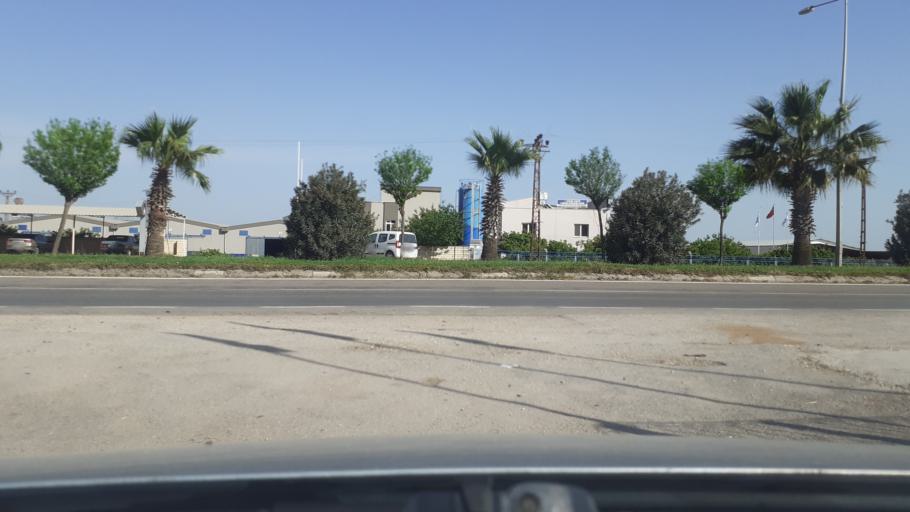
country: TR
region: Hatay
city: Kirikhan
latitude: 36.4914
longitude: 36.3697
